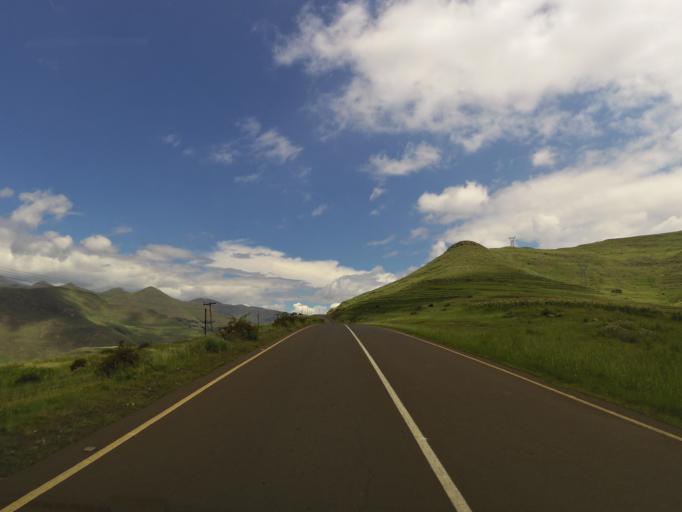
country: LS
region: Thaba-Tseka
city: Thaba-Tseka
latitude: -29.1298
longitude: 28.4925
